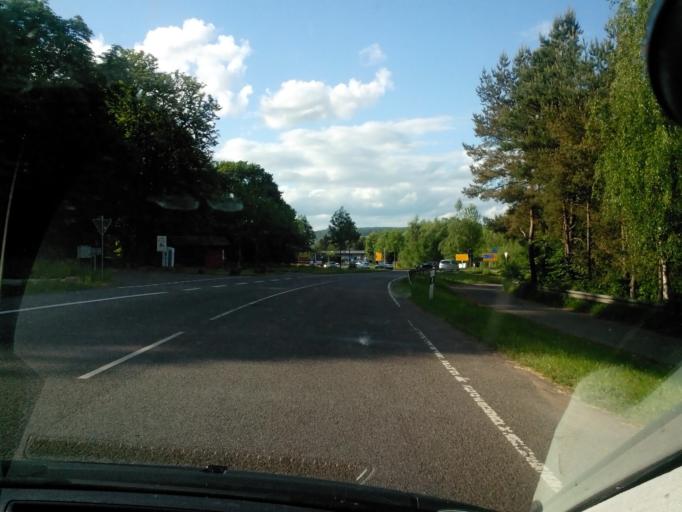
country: DE
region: Saarland
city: Rehlingen-Siersburg
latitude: 49.3632
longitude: 6.6874
